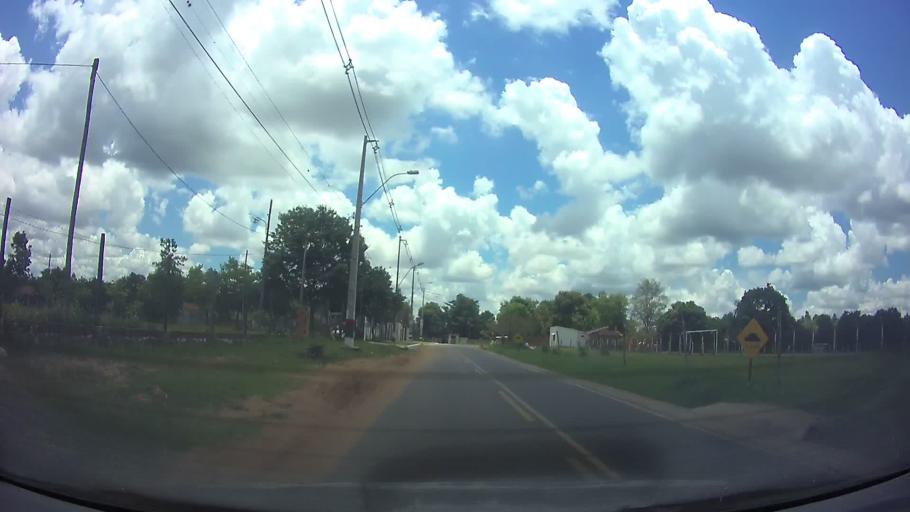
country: PY
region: Central
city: Capiata
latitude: -25.3427
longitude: -57.4187
